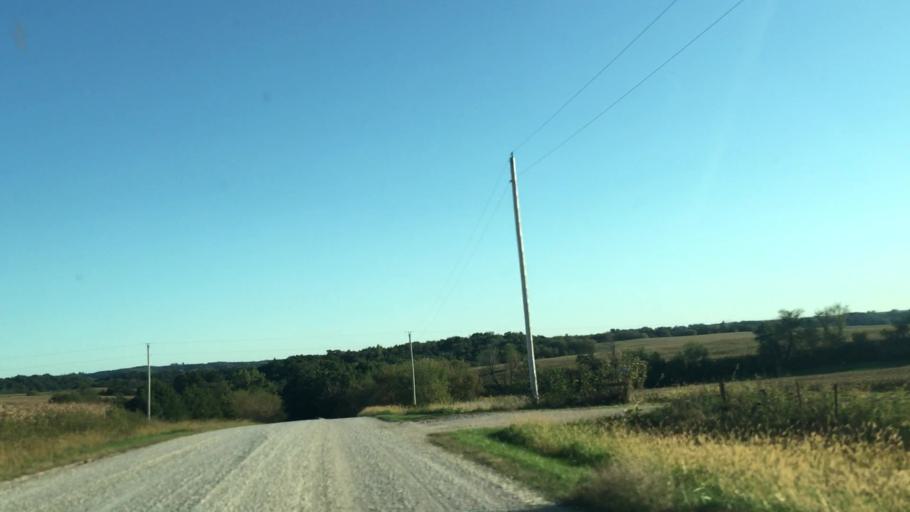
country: US
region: Minnesota
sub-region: Fillmore County
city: Preston
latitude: 43.7949
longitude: -92.0394
